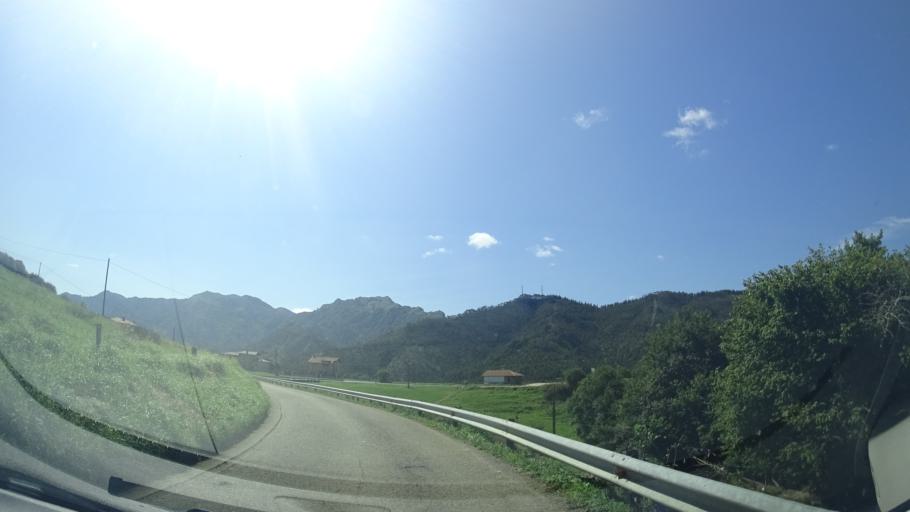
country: ES
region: Asturias
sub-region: Province of Asturias
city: Ribadesella
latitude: 43.4436
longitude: -5.0854
